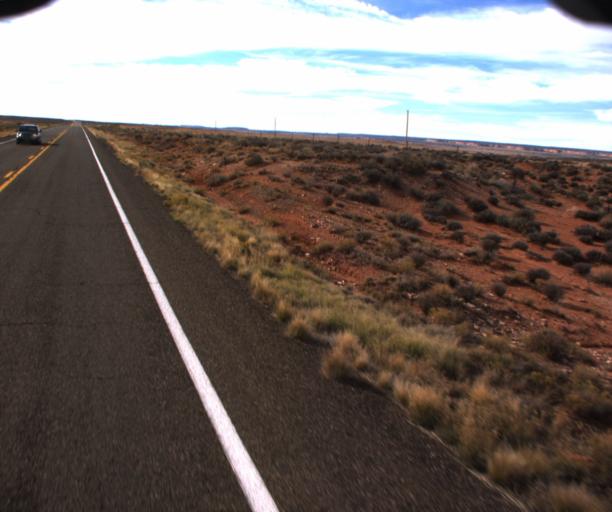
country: US
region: Arizona
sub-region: Coconino County
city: LeChee
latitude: 36.7560
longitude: -111.2850
